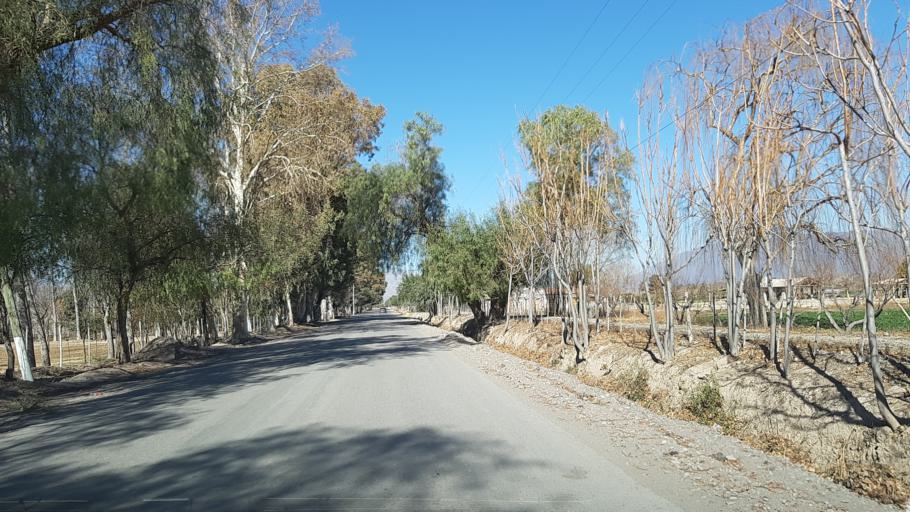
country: AR
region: San Juan
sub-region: Departamento de Zonda
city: Zonda
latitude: -31.4634
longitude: -68.7232
